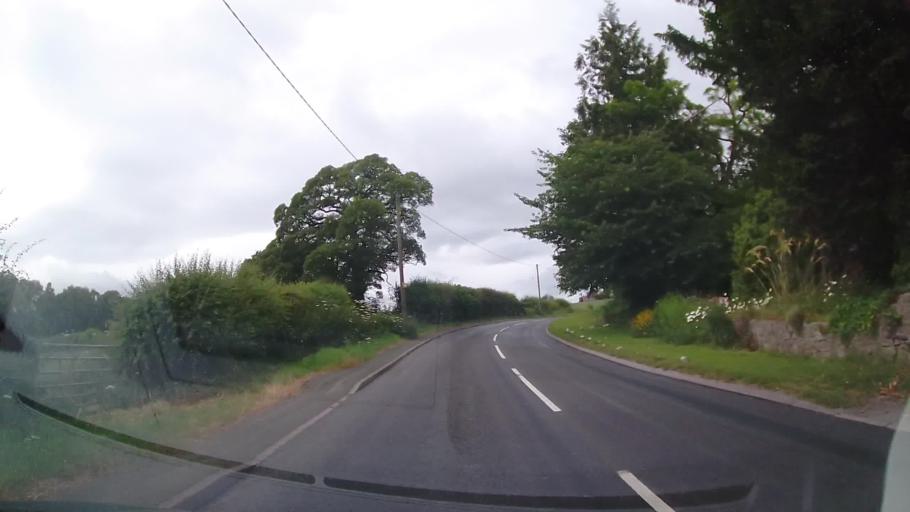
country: GB
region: England
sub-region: Shropshire
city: Gobowen
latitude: 52.9185
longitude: -3.0319
